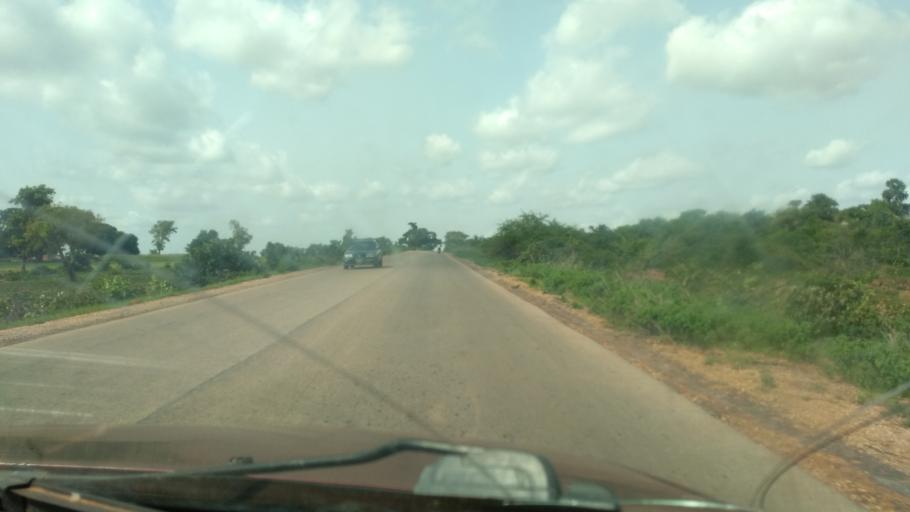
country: NG
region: Katsina
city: Sabuwa
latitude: 11.0532
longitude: 7.1639
